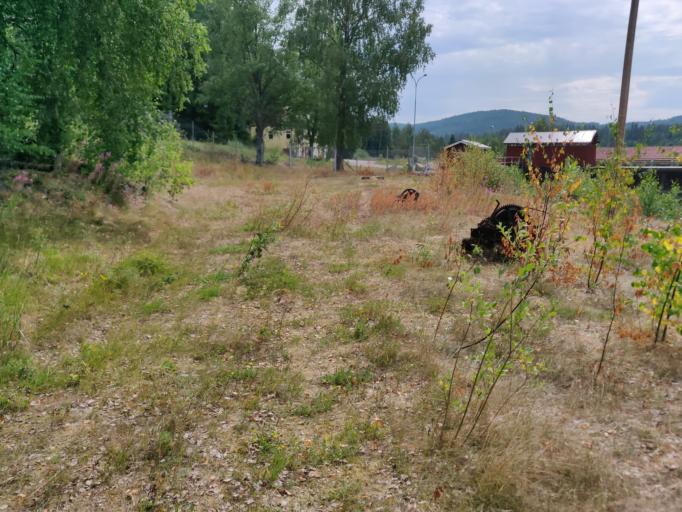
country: SE
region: Vaermland
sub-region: Munkfors Kommun
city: Munkfors
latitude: 59.9568
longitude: 13.5261
